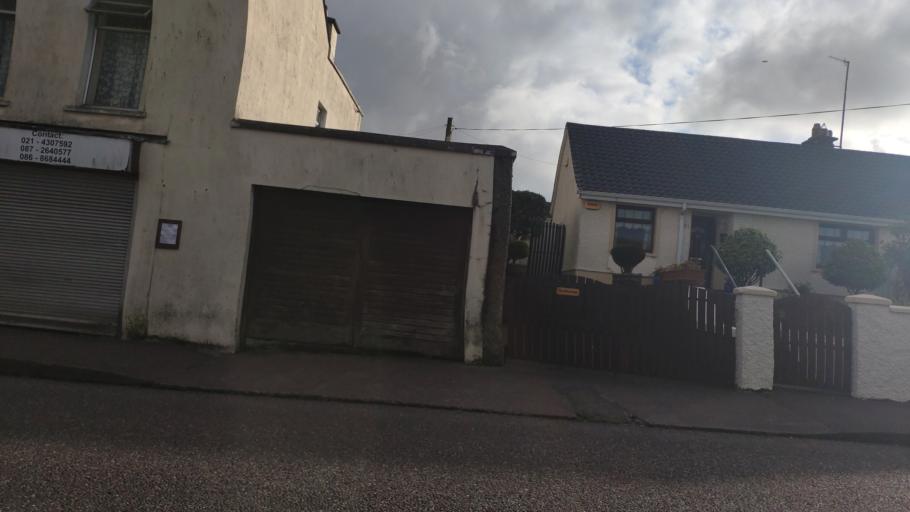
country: IE
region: Munster
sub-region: County Cork
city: Cork
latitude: 51.9113
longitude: -8.4872
